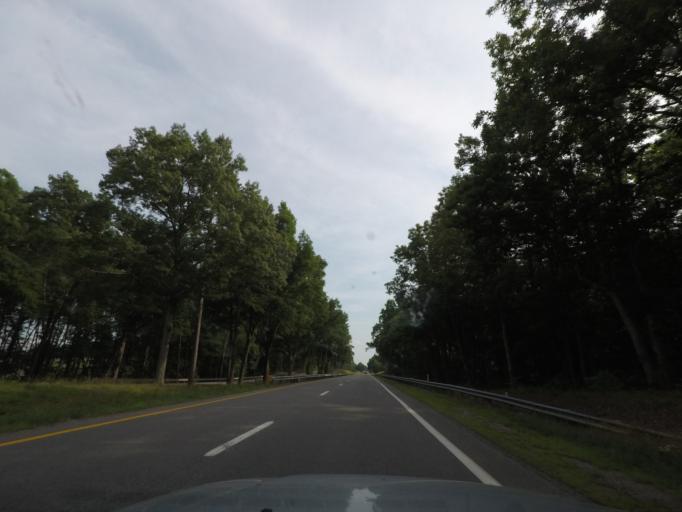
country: US
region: Virginia
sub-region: Charlotte County
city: Charlotte Court House
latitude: 36.9734
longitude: -78.4911
